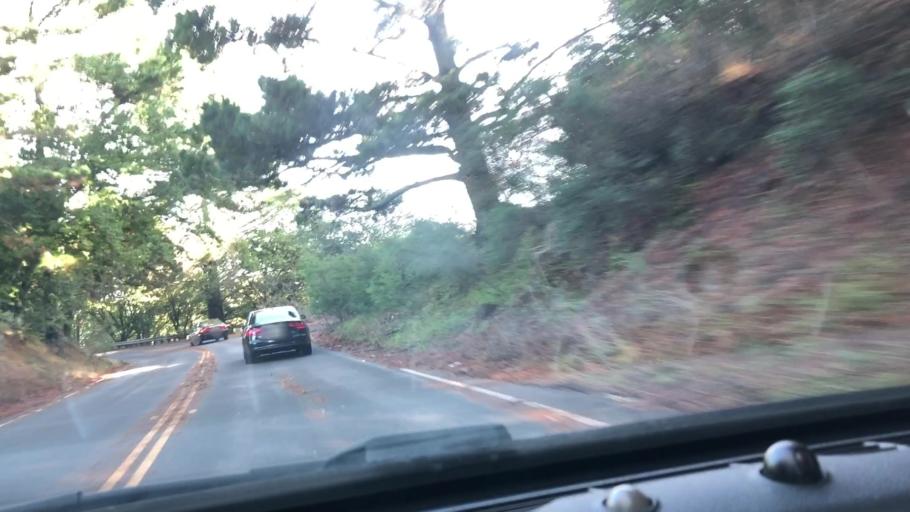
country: US
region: California
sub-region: Alameda County
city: Berkeley
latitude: 37.8828
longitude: -122.2361
